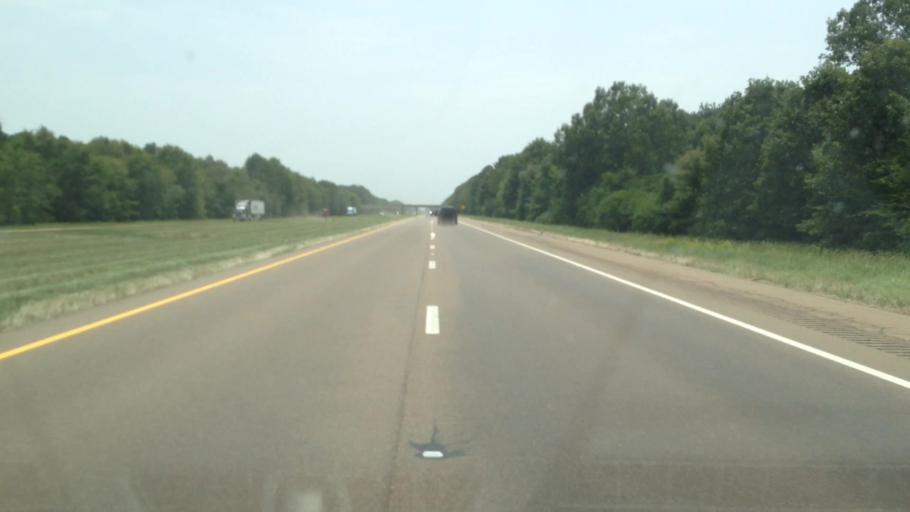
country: US
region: Texas
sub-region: Morris County
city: Naples
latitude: 33.3399
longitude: -94.6635
